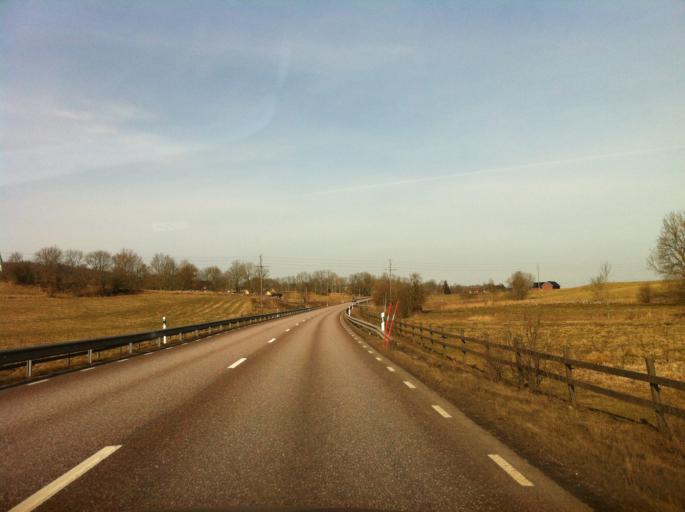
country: SE
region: Vaestra Goetaland
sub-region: Skovde Kommun
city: Skultorp
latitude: 58.2881
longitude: 13.8051
